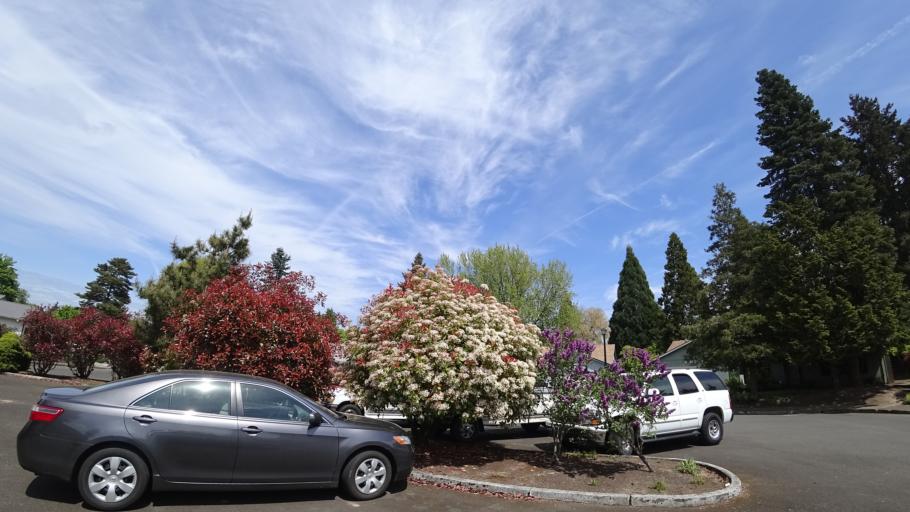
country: US
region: Oregon
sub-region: Washington County
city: Aloha
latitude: 45.4706
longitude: -122.8858
